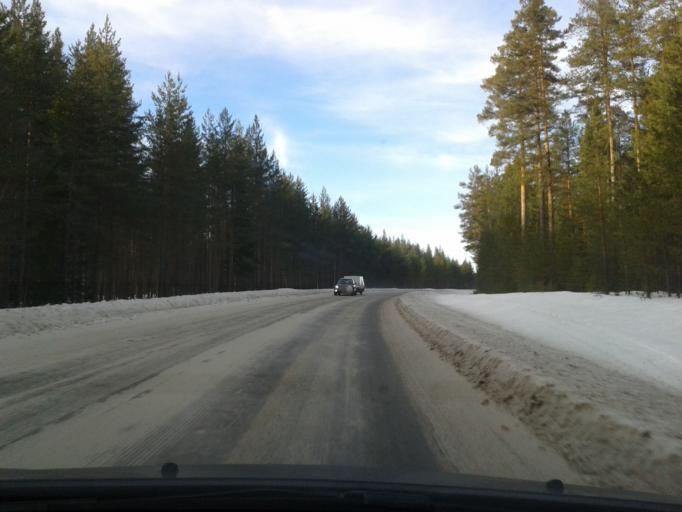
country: SE
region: Vaesternorrland
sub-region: OErnskoeldsviks Kommun
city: Bredbyn
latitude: 63.5324
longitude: 17.9679
